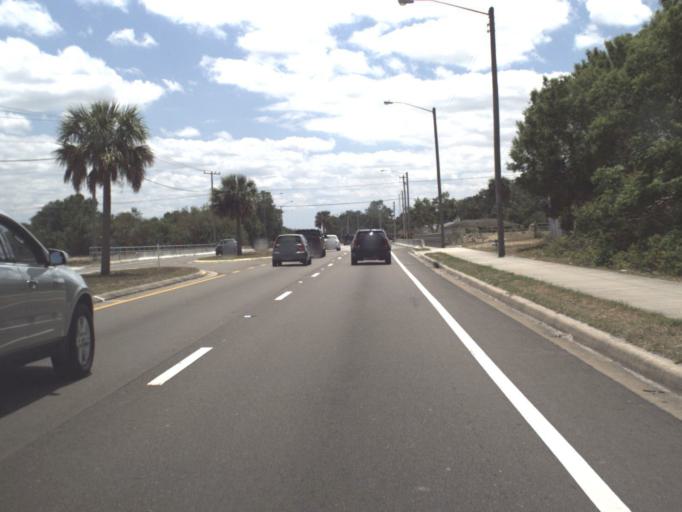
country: US
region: Florida
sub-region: Brevard County
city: Palm Bay
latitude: 28.0142
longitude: -80.6223
